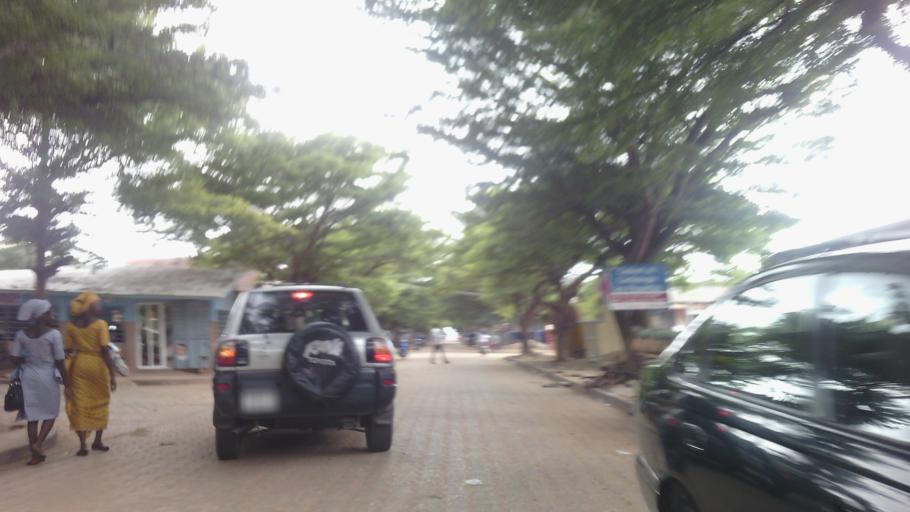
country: BJ
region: Atlantique
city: Abomey-Calavi
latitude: 6.4751
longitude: 2.3563
